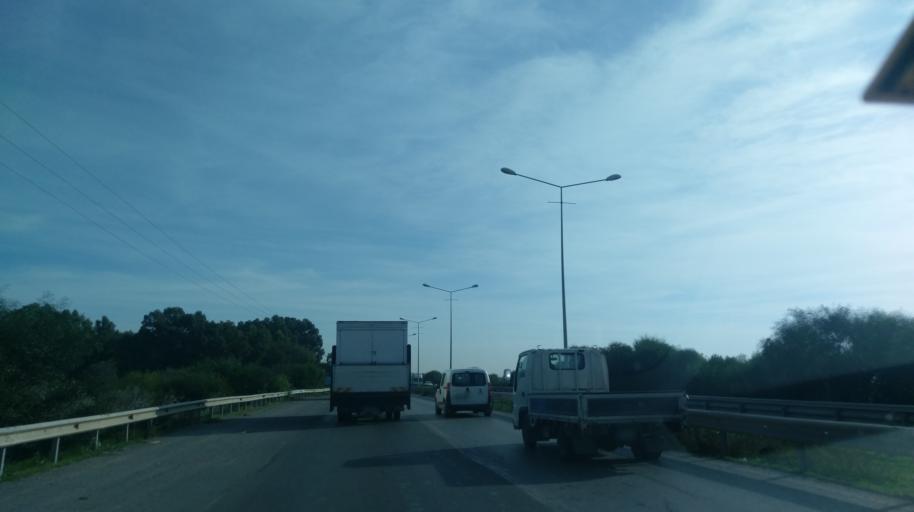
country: CY
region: Lefkosia
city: Nicosia
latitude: 35.2135
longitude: 33.3881
